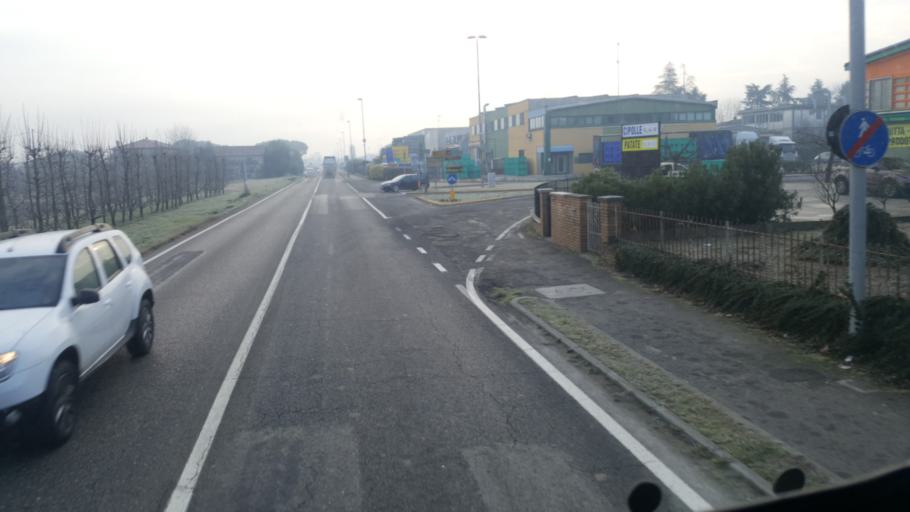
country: IT
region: Emilia-Romagna
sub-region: Provincia di Ravenna
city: Bagnacavallo
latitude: 44.4107
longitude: 11.9918
